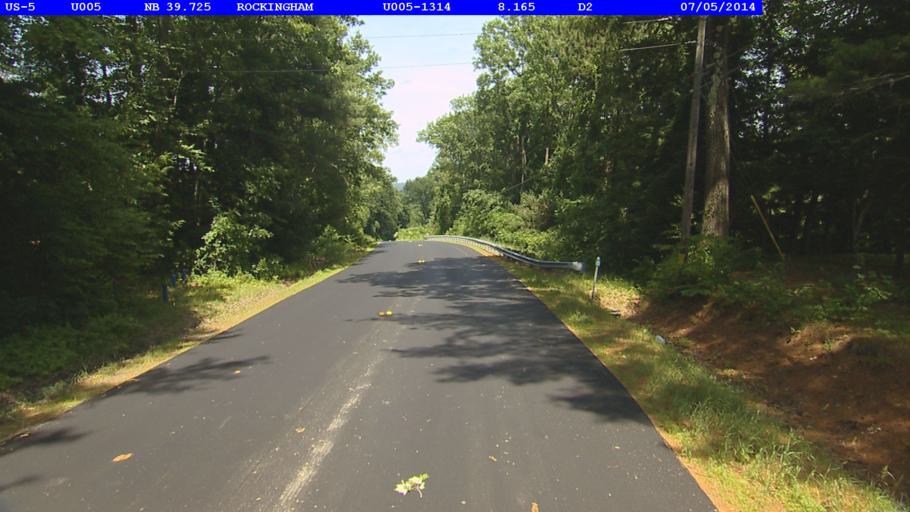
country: US
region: New Hampshire
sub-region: Sullivan County
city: Charlestown
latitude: 43.2244
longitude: -72.4411
